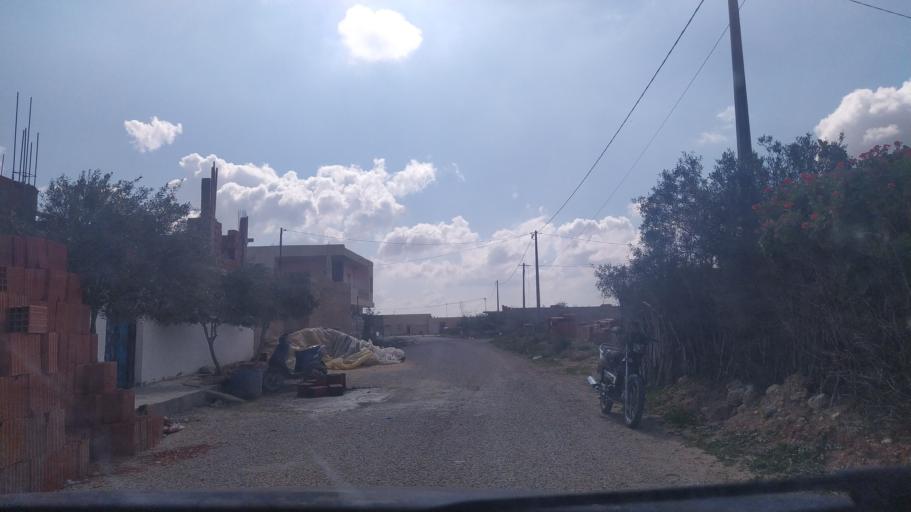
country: TN
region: Al Munastir
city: Sidi Bin Nur
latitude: 35.5282
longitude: 10.9428
